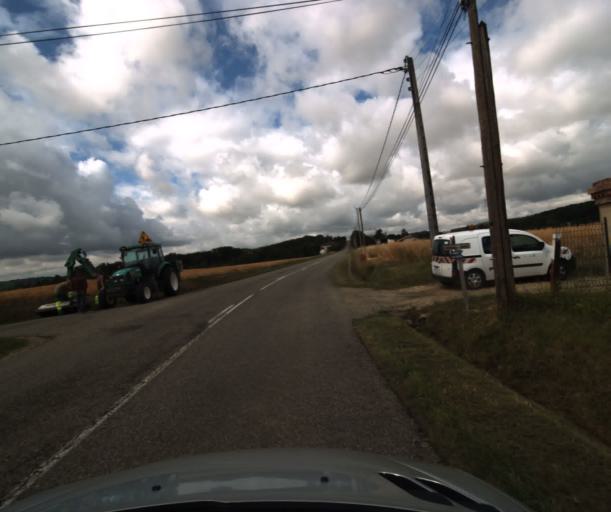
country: FR
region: Midi-Pyrenees
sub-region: Departement du Tarn-et-Garonne
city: Lavit
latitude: 43.9727
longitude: 0.9505
